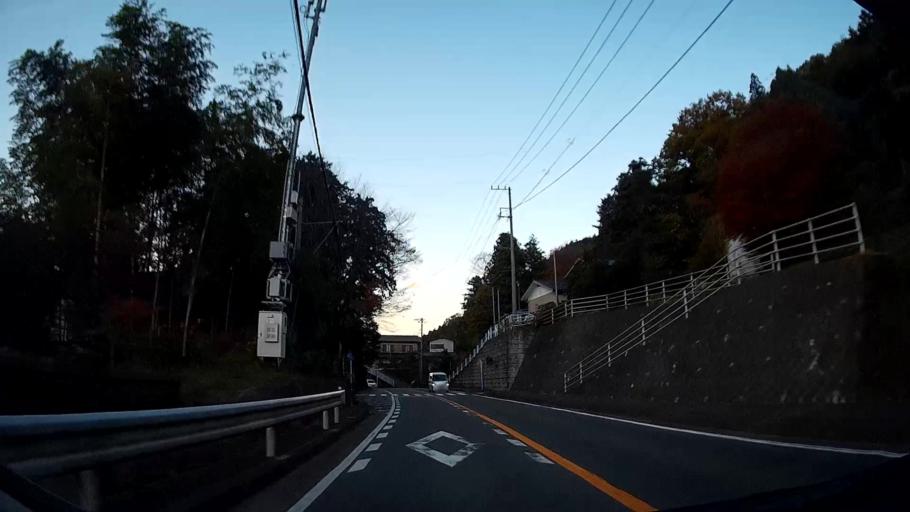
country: JP
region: Yamanashi
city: Uenohara
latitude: 35.5707
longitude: 139.2215
